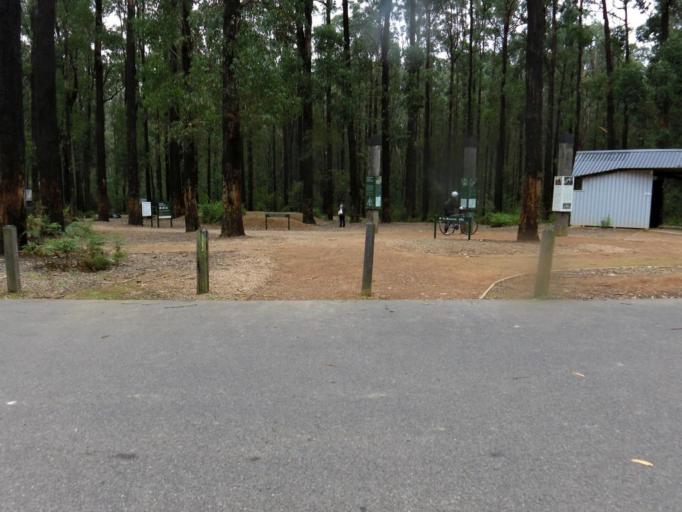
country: AU
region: Victoria
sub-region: Murrindindi
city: Kinglake West
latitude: -37.4932
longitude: 145.2508
